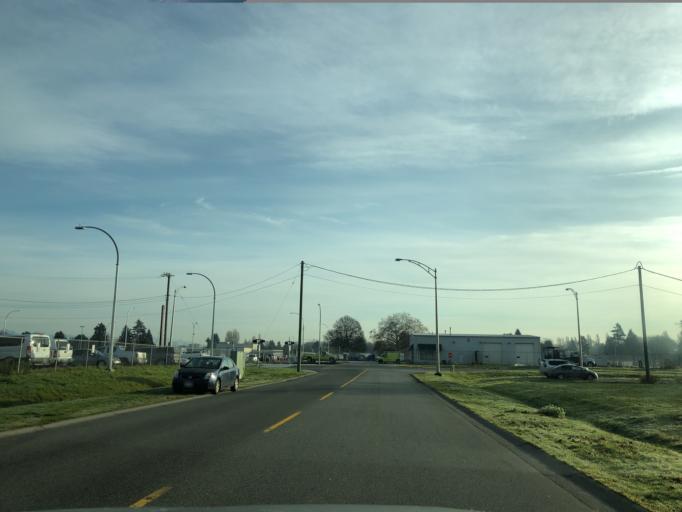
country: CA
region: British Columbia
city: Richmond
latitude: 49.1904
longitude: -123.1549
